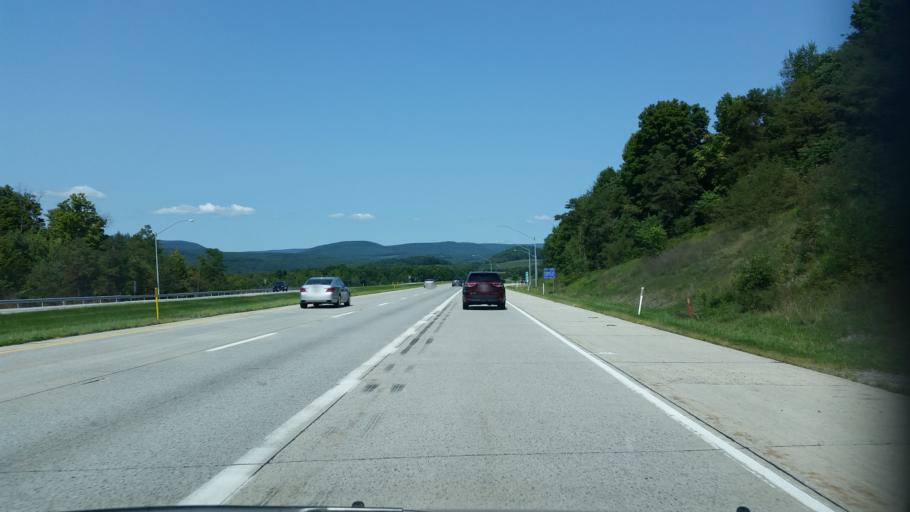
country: US
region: Pennsylvania
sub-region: Blair County
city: Bellwood
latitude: 40.5924
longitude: -78.3158
